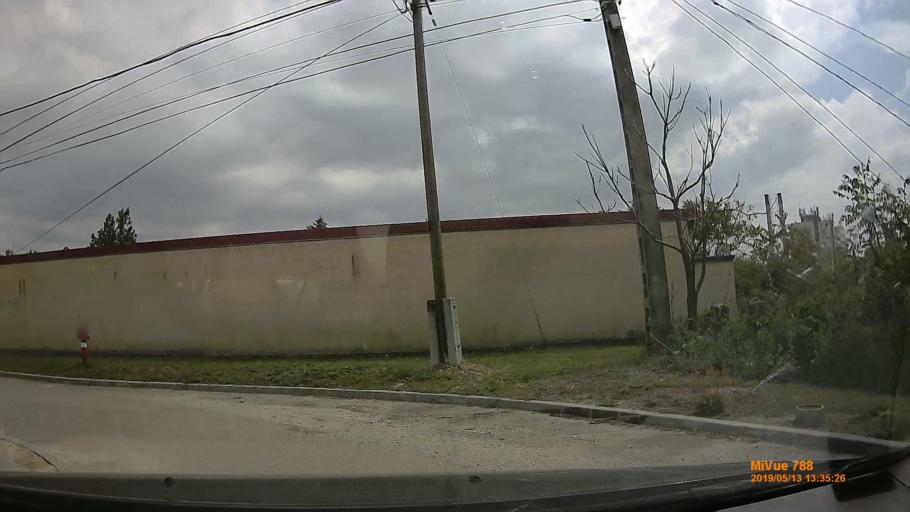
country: HU
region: Budapest
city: Budapest XXII. keruelet
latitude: 47.4101
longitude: 19.0075
